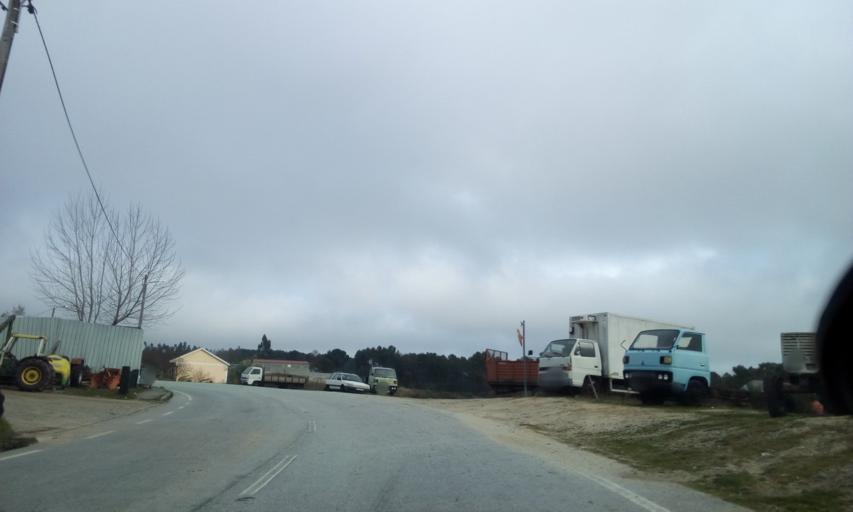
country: PT
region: Guarda
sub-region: Fornos de Algodres
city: Fornos de Algodres
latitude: 40.7211
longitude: -7.4910
